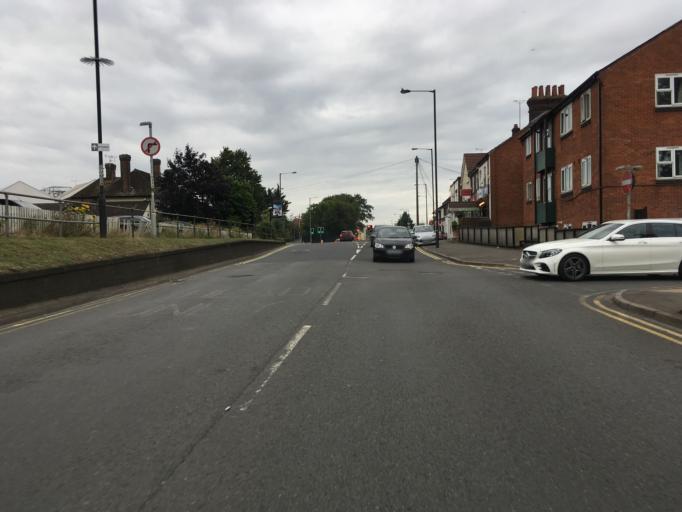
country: GB
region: England
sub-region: Central Bedfordshire
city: Dunstable
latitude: 51.8933
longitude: -0.5310
